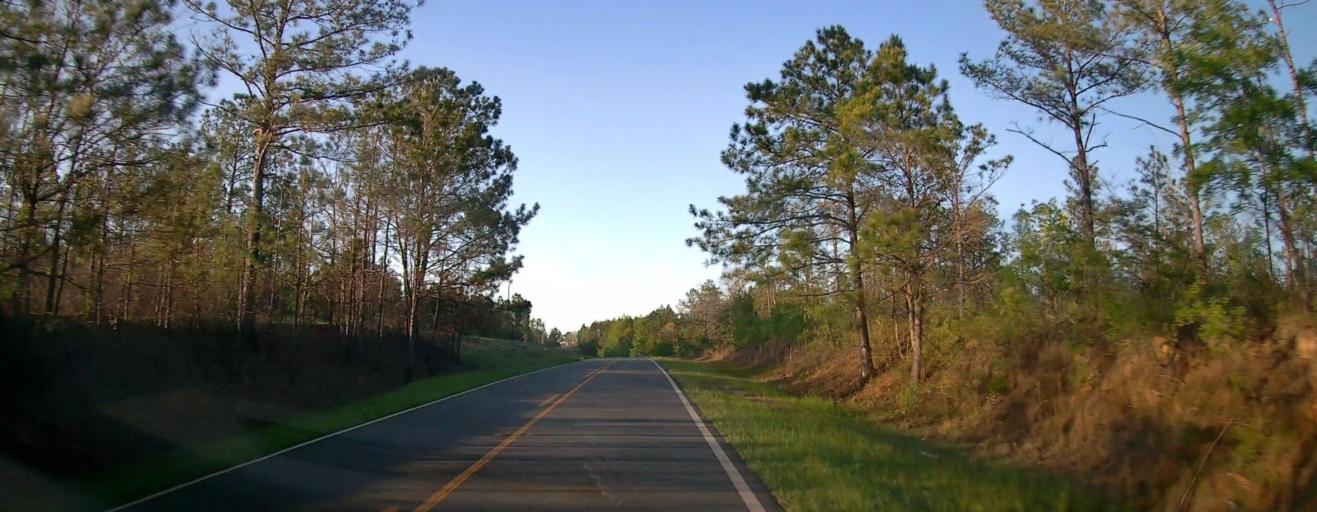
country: US
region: Georgia
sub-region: Marion County
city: Buena Vista
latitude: 32.4476
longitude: -84.4258
